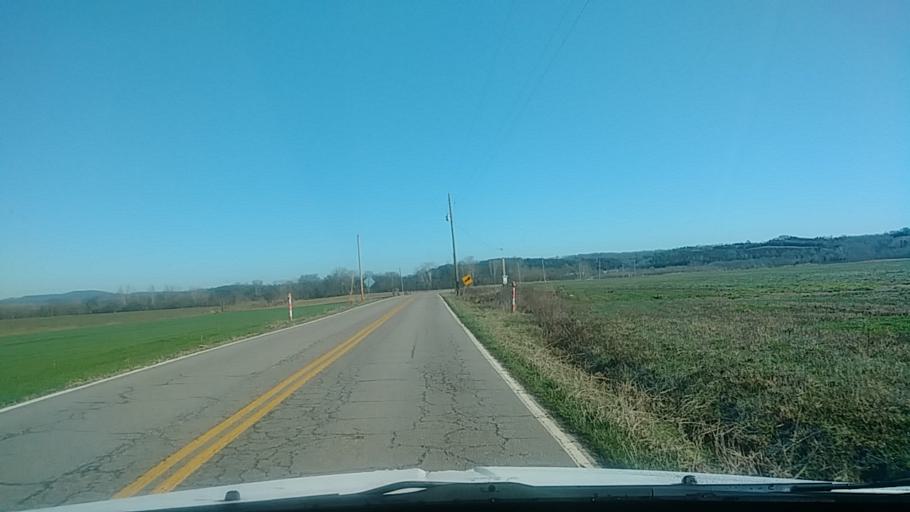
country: US
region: Tennessee
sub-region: Jefferson County
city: White Pine
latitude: 36.1640
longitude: -83.1628
